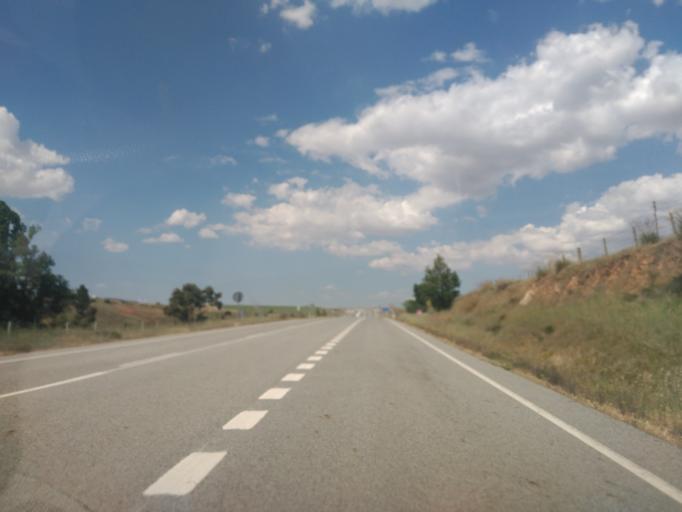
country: ES
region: Castille and Leon
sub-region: Provincia de Salamanca
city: Belena
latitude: 40.7642
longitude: -5.6268
